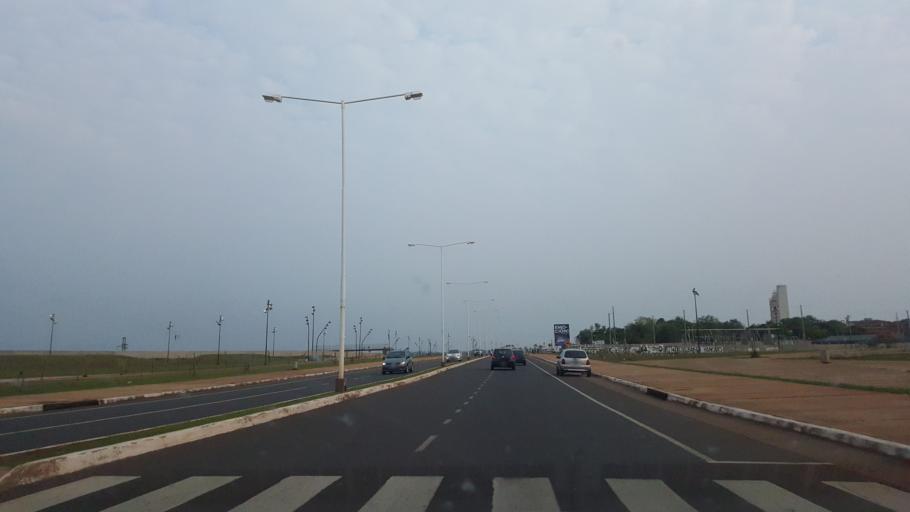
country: AR
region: Misiones
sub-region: Departamento de Capital
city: Posadas
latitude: -27.3763
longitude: -55.8858
